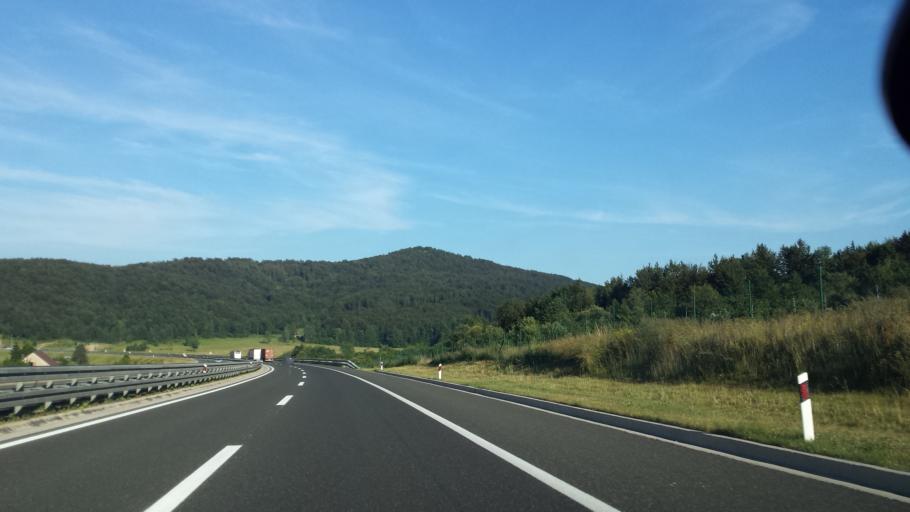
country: HR
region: Primorsko-Goranska
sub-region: Grad Delnice
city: Delnice
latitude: 45.3822
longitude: 14.8441
